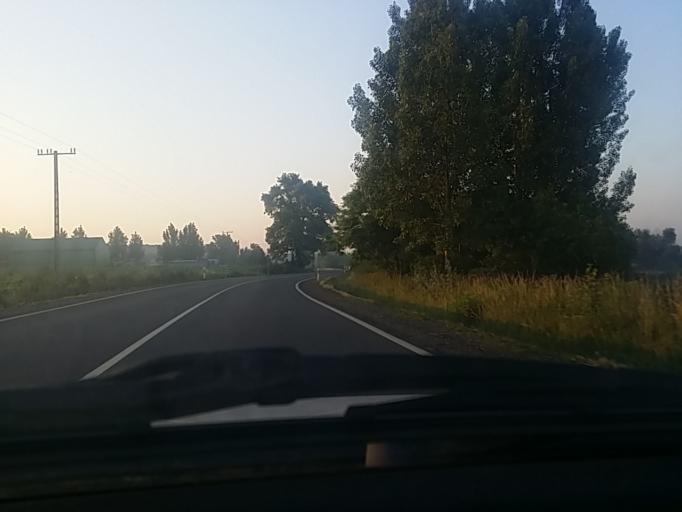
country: HU
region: Pest
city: Gyomro
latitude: 47.4463
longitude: 19.3939
